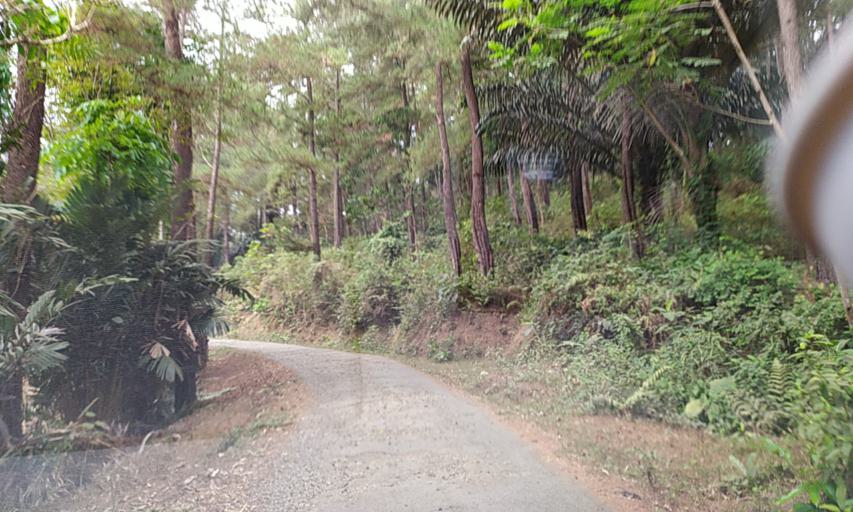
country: ID
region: Central Java
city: Cipeusing
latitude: -7.2503
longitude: 108.8181
